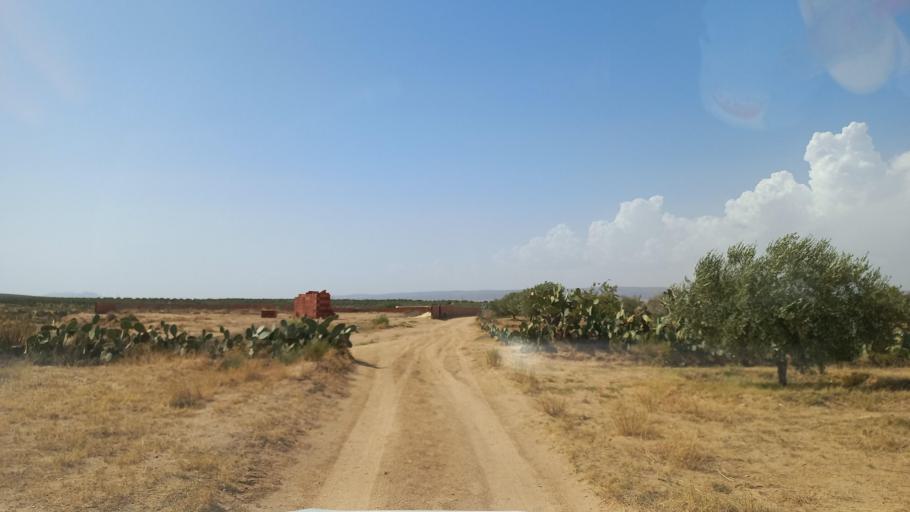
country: TN
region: Al Qasrayn
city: Kasserine
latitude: 35.2095
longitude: 9.0388
